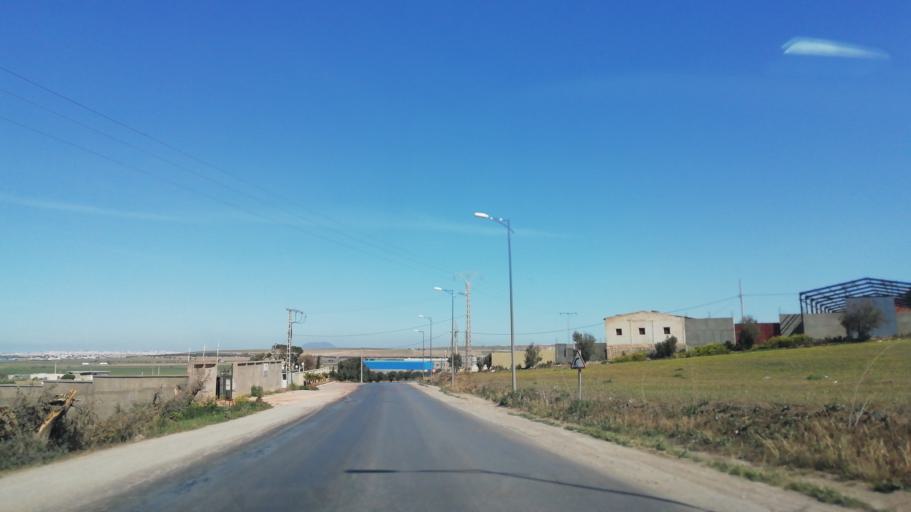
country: DZ
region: Oran
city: Es Senia
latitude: 35.5543
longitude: -0.5725
